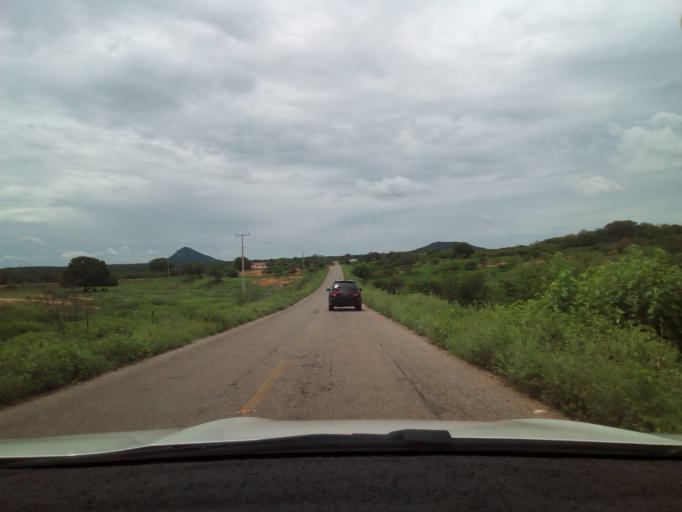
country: BR
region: Rio Grande do Norte
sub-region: Patu
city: Patu
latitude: -6.1390
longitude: -37.7432
